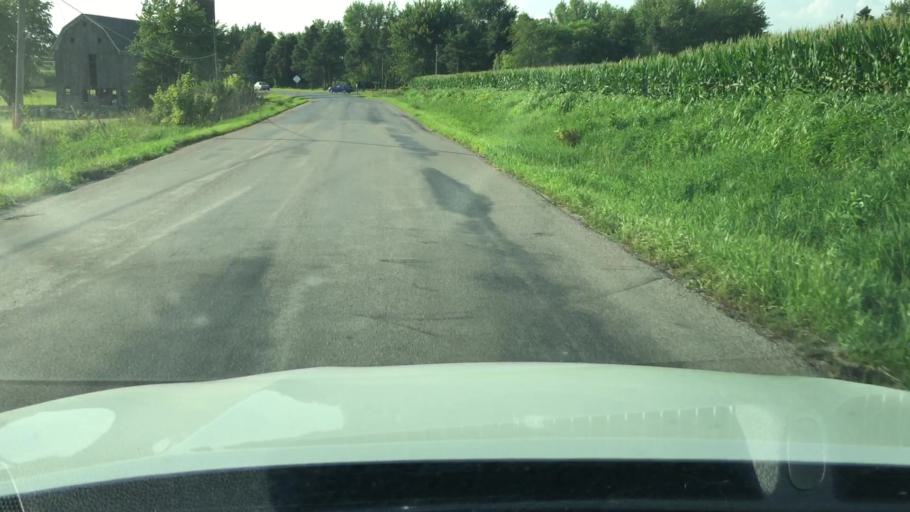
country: US
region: Iowa
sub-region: Johnson County
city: North Liberty
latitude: 41.8137
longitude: -91.6155
